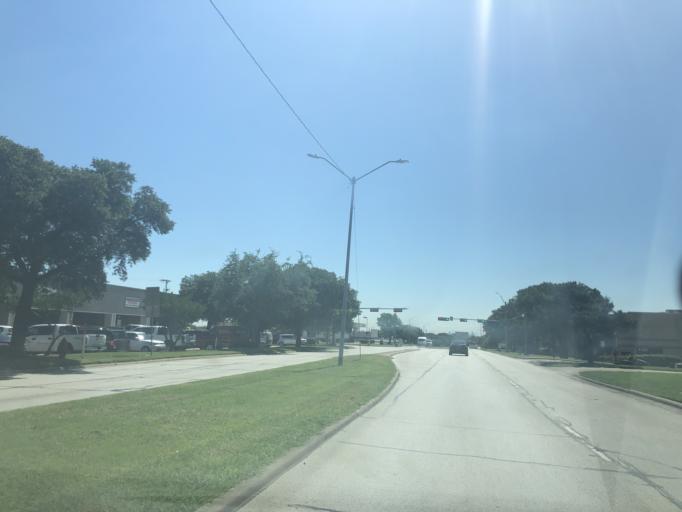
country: US
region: Texas
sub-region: Dallas County
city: Grand Prairie
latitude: 32.7853
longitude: -97.0432
